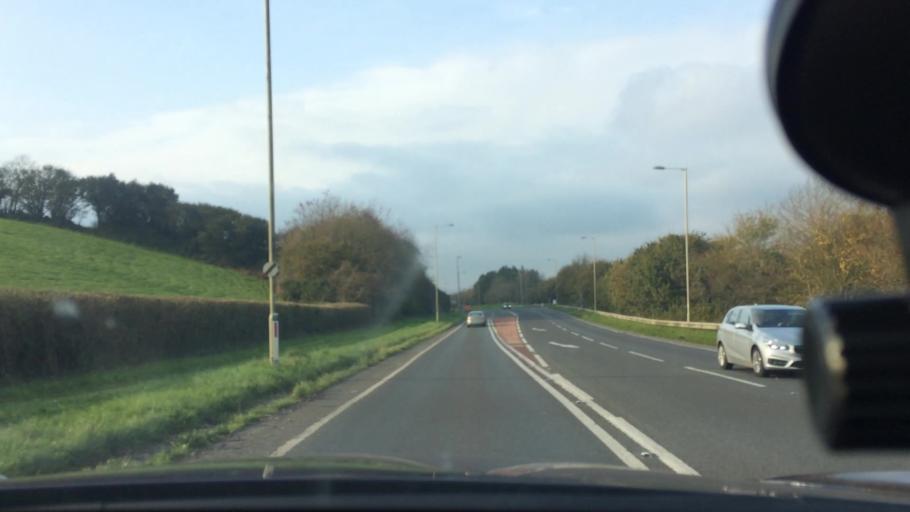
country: GB
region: England
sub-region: Devon
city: Axminster
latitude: 50.7653
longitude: -2.9762
